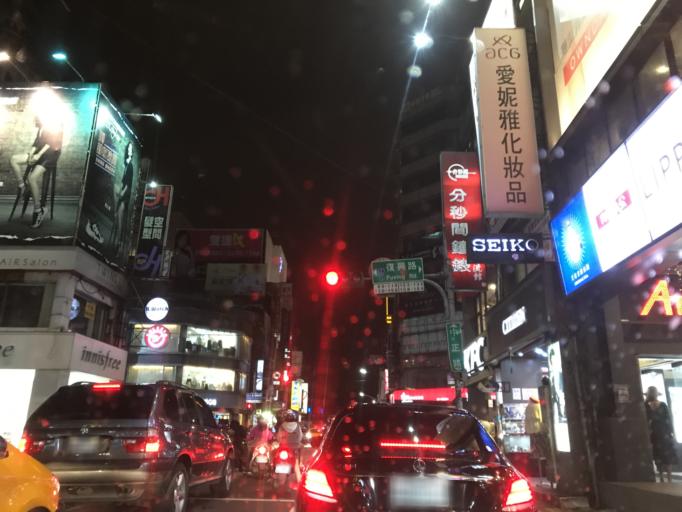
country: TW
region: Taiwan
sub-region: Taoyuan
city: Taoyuan
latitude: 24.9907
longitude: 121.3128
